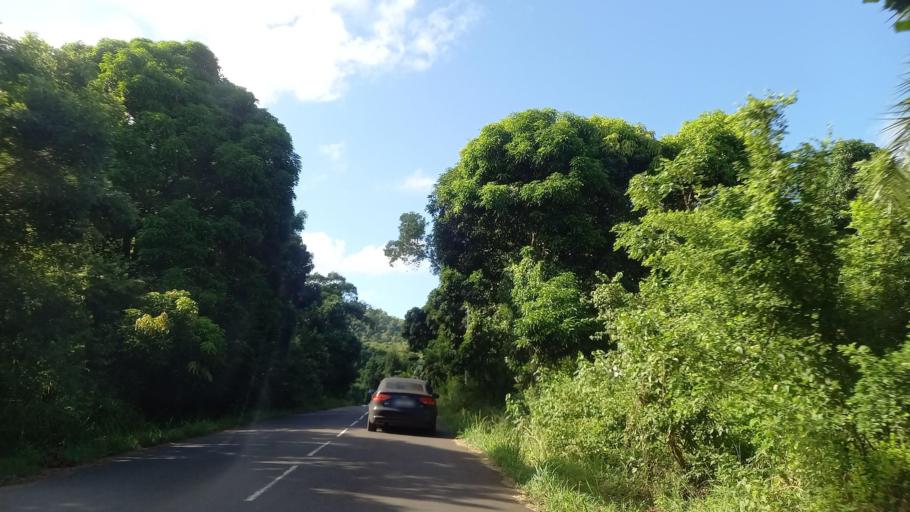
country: YT
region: Kani-Keli
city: Kani Keli
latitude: -12.9626
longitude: 45.1123
